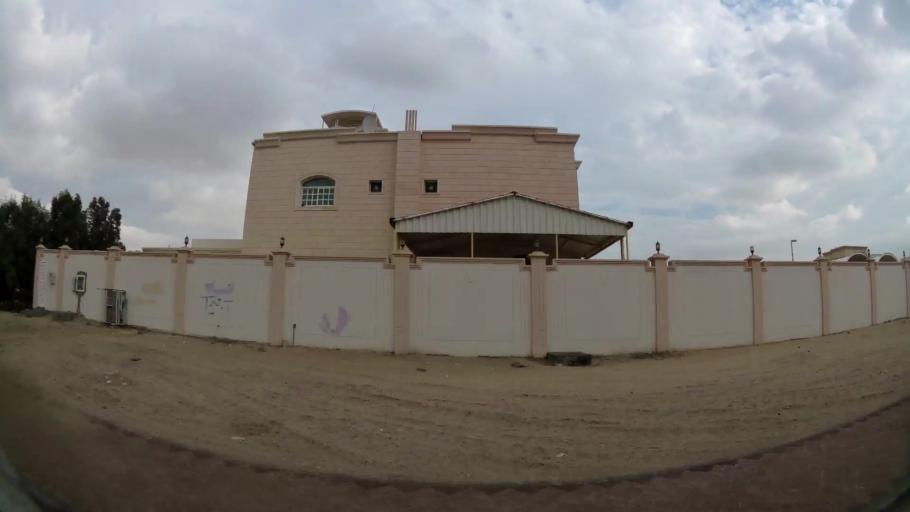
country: AE
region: Abu Dhabi
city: Abu Dhabi
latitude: 24.3444
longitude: 54.6197
